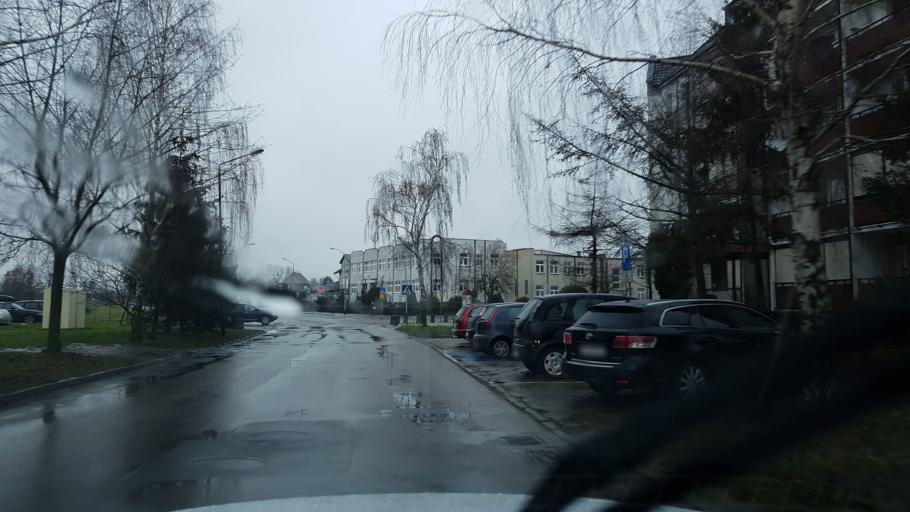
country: PL
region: West Pomeranian Voivodeship
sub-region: Powiat stargardzki
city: Stargard Szczecinski
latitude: 53.3154
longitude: 15.0340
